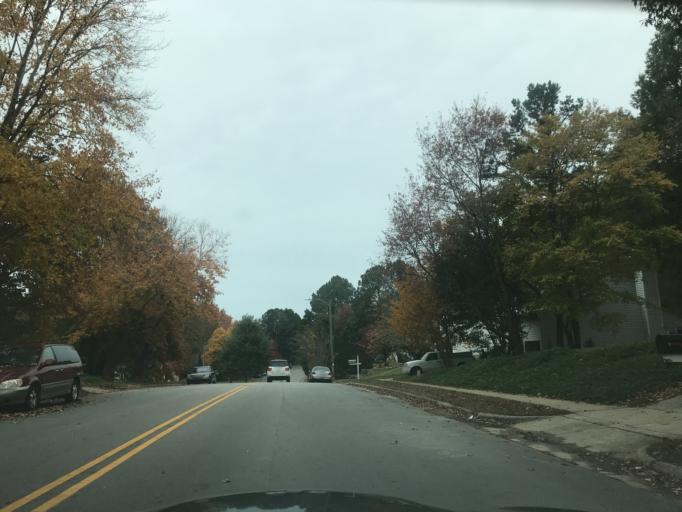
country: US
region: North Carolina
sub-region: Wake County
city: West Raleigh
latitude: 35.8859
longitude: -78.6419
